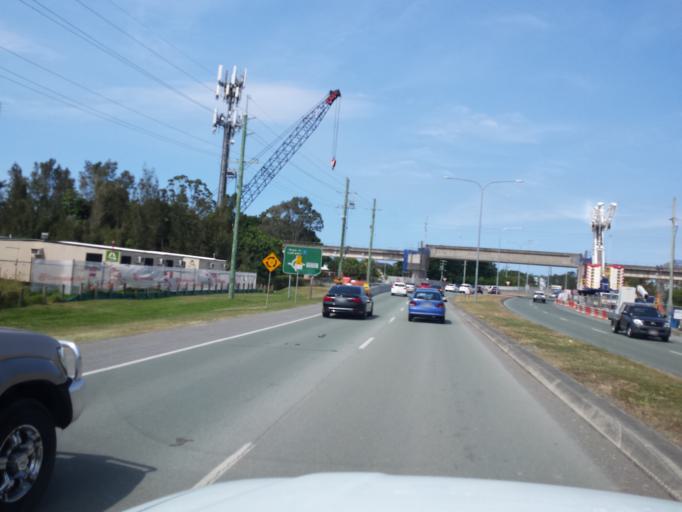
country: AU
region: Queensland
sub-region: Gold Coast
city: Oxenford
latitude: -27.8811
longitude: 153.3303
